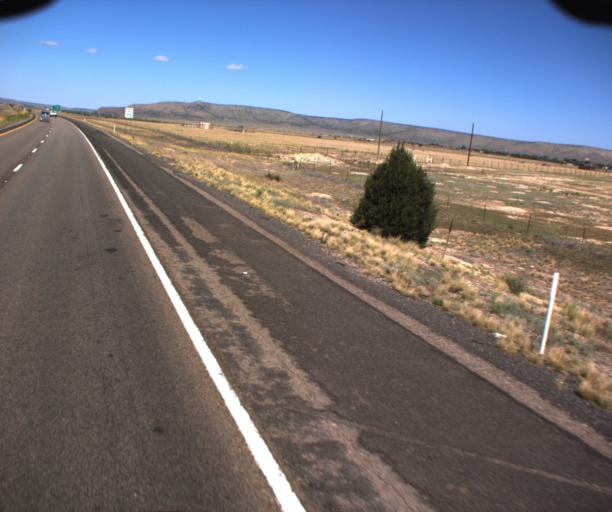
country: US
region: Arizona
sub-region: Yavapai County
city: Paulden
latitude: 35.3153
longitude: -112.8669
